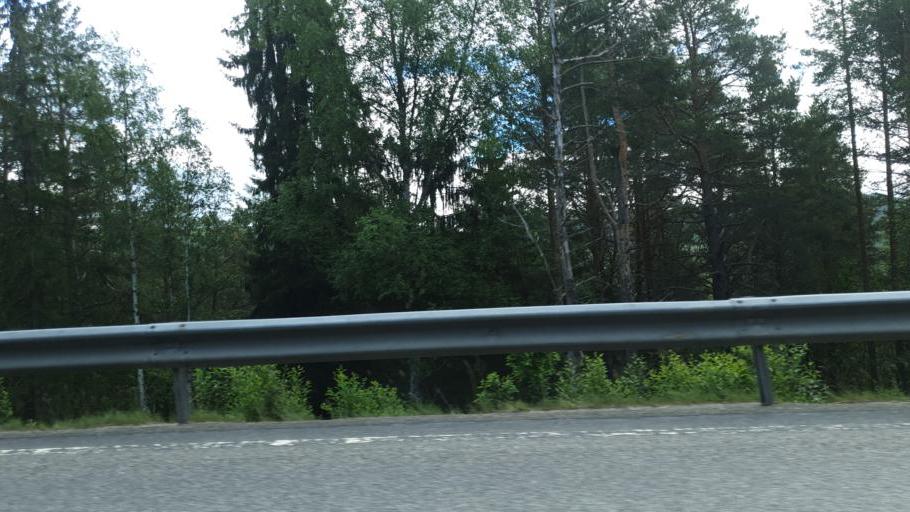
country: NO
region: Sor-Trondelag
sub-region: Rennebu
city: Berkak
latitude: 62.6650
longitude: 9.8959
